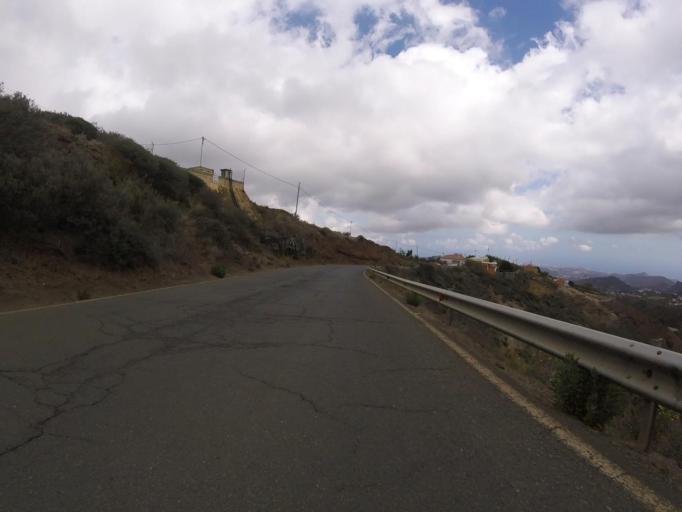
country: ES
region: Canary Islands
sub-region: Provincia de Las Palmas
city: Vega de San Mateo
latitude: 27.9980
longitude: -15.5671
